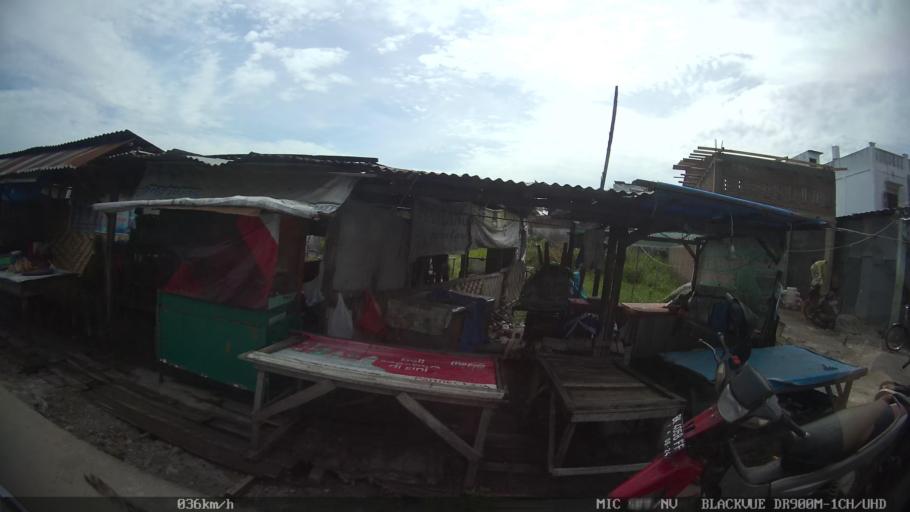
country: ID
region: North Sumatra
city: Percut
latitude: 3.6162
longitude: 98.7998
